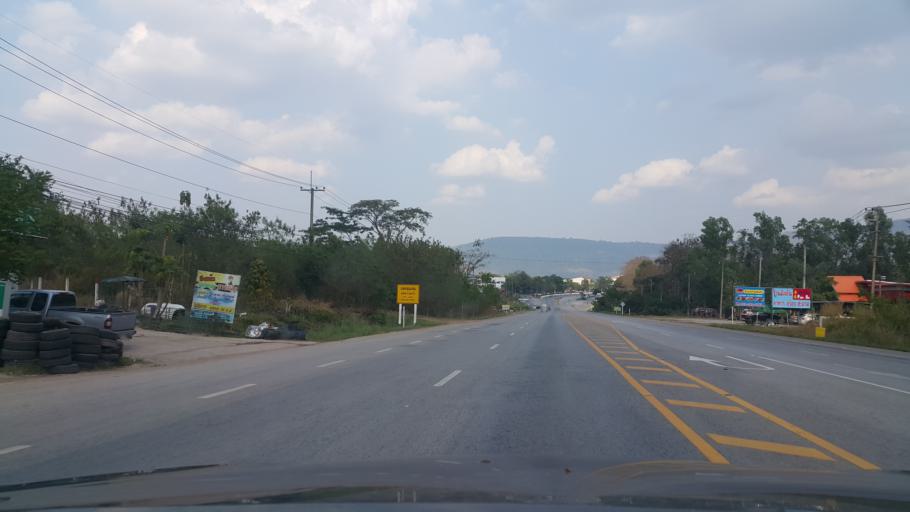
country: TH
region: Phitsanulok
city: Wang Thong
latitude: 16.8707
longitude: 100.6672
